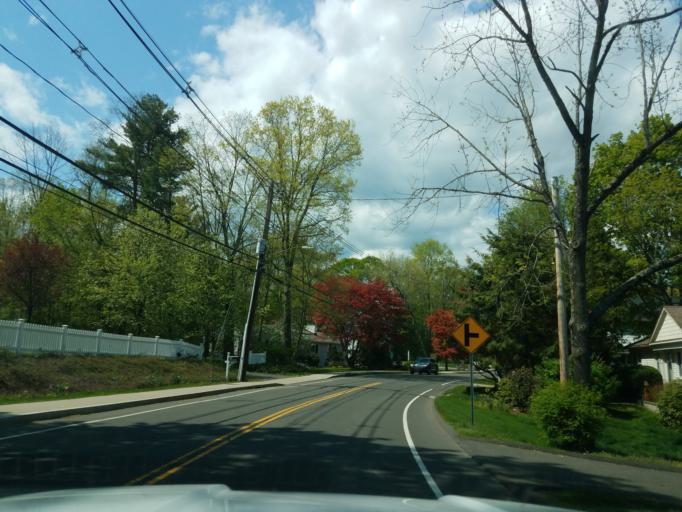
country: US
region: Connecticut
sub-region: Fairfield County
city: New Canaan
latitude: 41.1389
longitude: -73.4829
